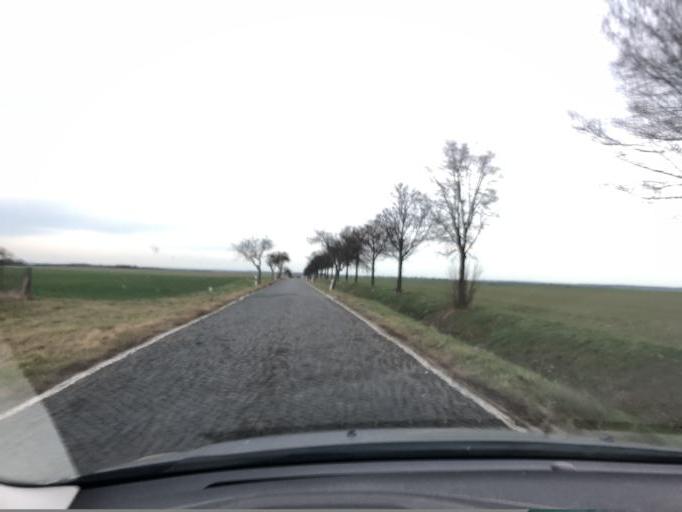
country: DE
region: Saxony-Anhalt
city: Laucha
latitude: 51.1804
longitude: 11.6446
